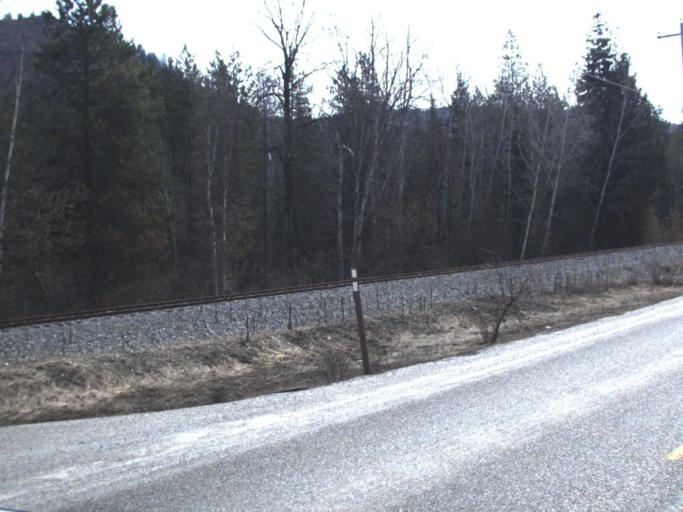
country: US
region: Washington
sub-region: Stevens County
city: Chewelah
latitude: 48.6459
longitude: -117.3775
